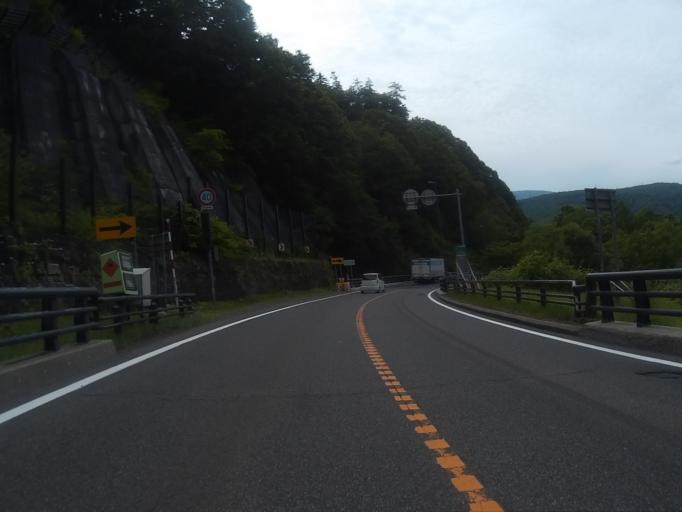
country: JP
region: Hokkaido
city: Sapporo
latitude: 42.9013
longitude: 141.1277
